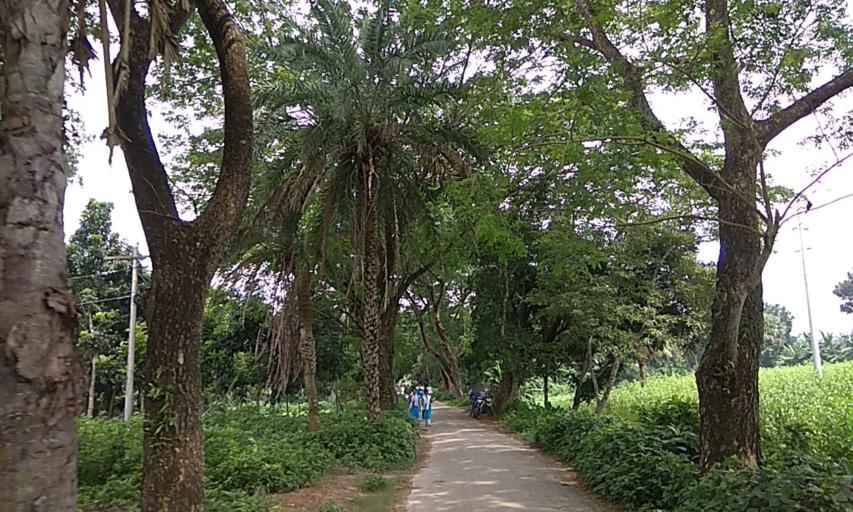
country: BD
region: Dhaka
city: Faridpur
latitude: 23.5345
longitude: 89.9693
